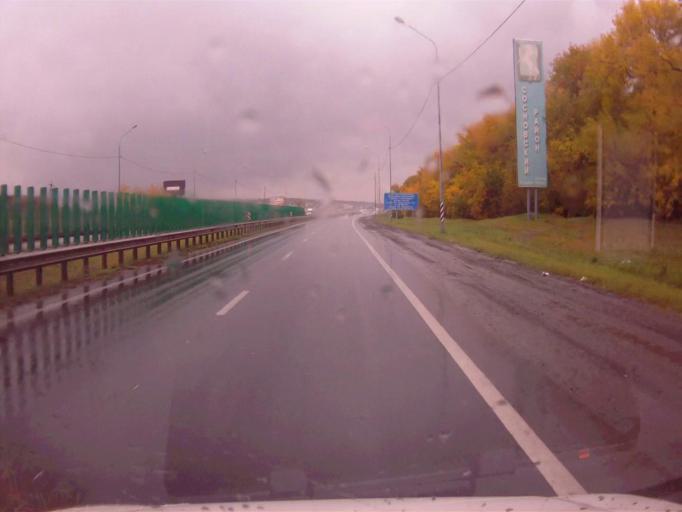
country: RU
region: Chelyabinsk
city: Dolgoderevenskoye
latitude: 55.2672
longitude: 61.3455
